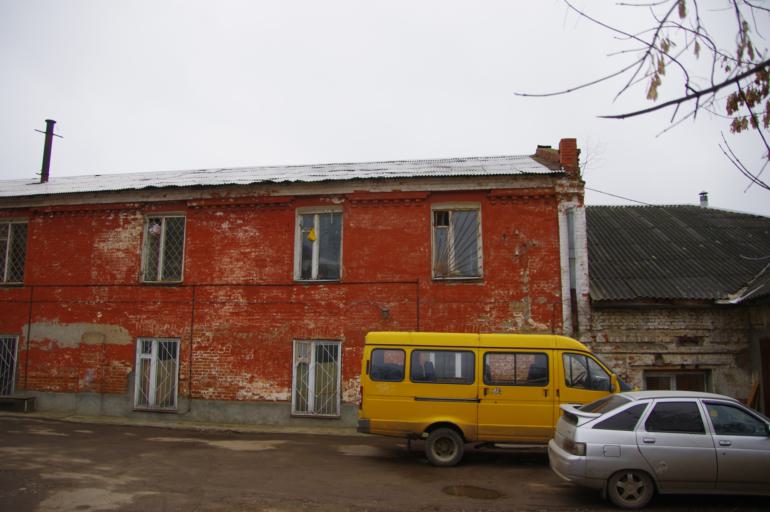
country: RU
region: Moskovskaya
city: Opalikha
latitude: 55.8426
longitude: 37.2538
